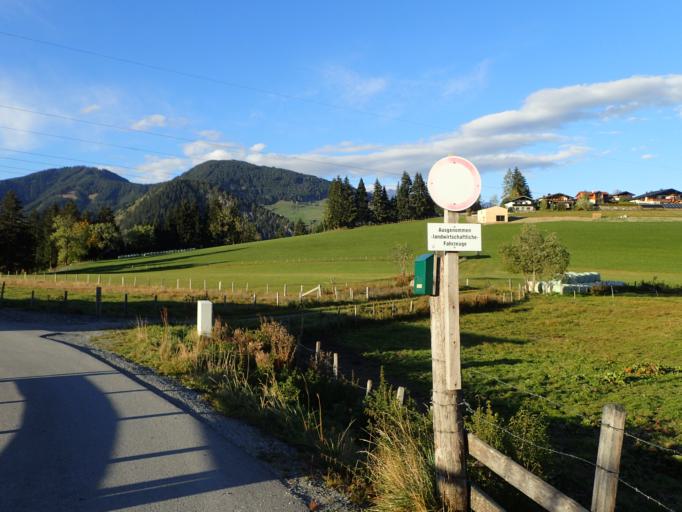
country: AT
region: Salzburg
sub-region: Politischer Bezirk Zell am See
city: Taxenbach
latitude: 47.2909
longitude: 12.9964
